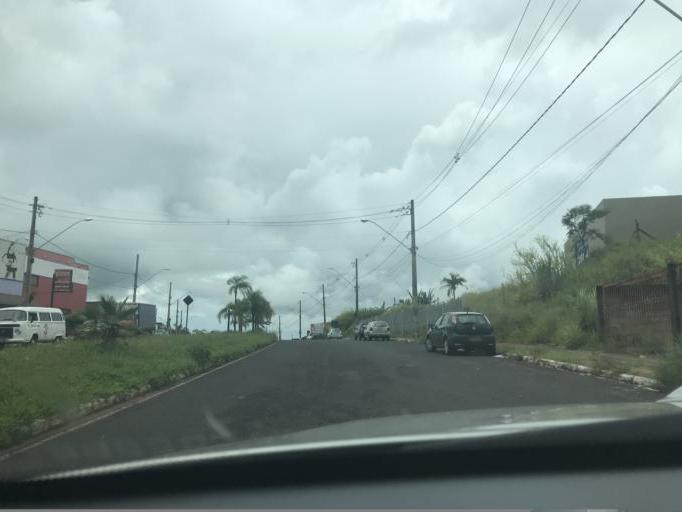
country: BR
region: Minas Gerais
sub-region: Araxa
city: Araxa
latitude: -19.5805
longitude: -46.9376
